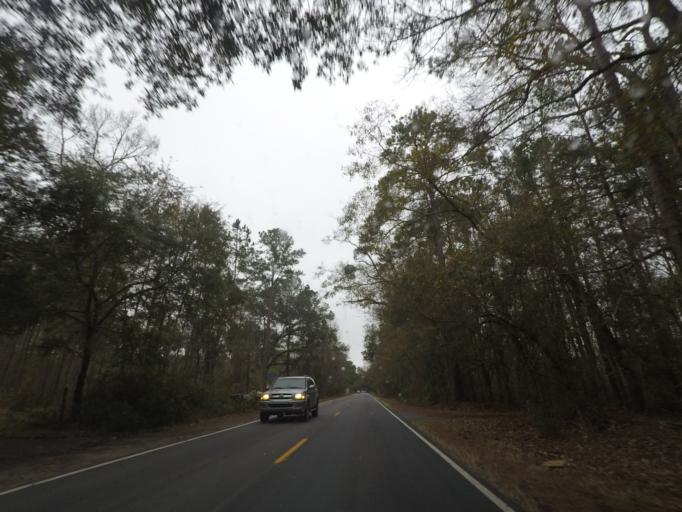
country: US
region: South Carolina
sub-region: Charleston County
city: Ravenel
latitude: 32.7383
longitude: -80.3503
